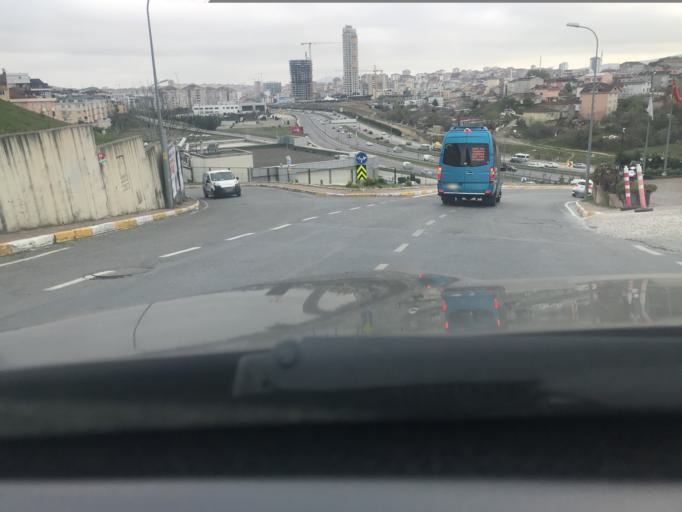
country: TR
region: Istanbul
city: Umraniye
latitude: 41.0368
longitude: 29.1606
